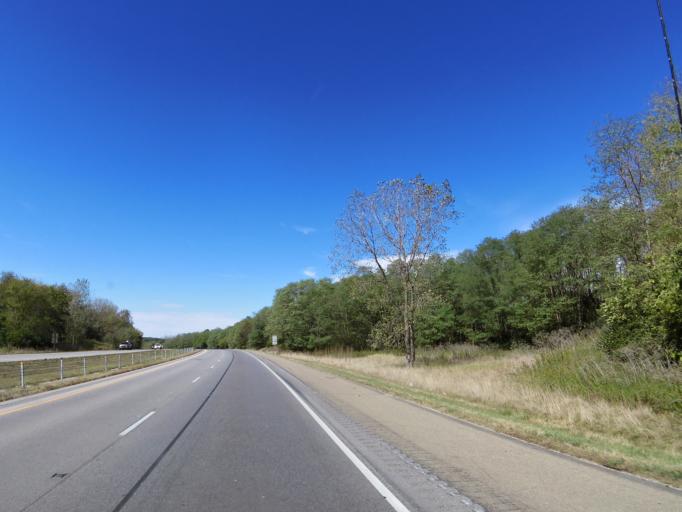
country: US
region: Illinois
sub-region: Vermilion County
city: Oakwood
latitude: 40.1266
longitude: -87.7189
